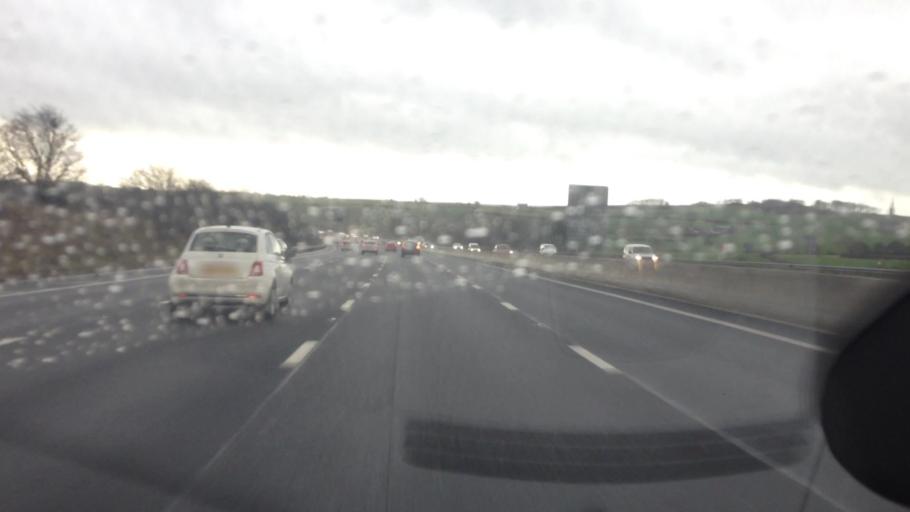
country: GB
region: England
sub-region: City and Borough of Wakefield
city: Ossett
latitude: 53.7014
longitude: -1.5552
